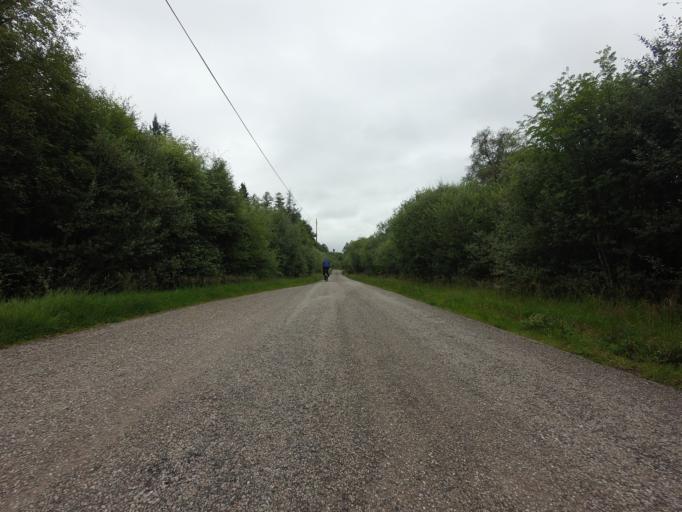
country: GB
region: Scotland
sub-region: Highland
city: Evanton
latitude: 57.9725
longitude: -4.4139
